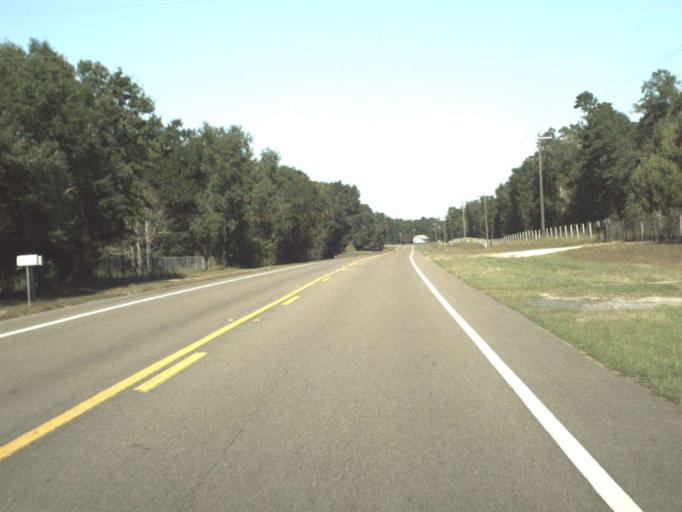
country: US
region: Florida
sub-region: Walton County
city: Freeport
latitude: 30.5829
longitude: -85.9348
